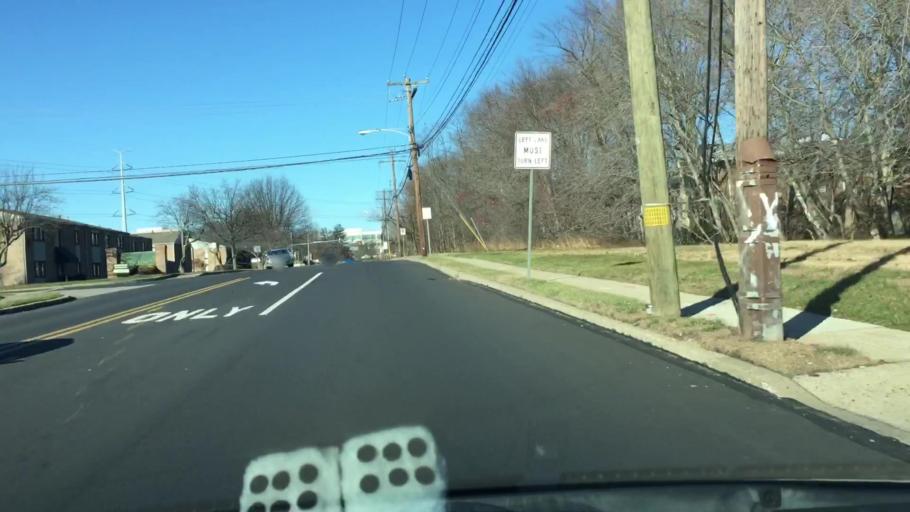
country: US
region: Pennsylvania
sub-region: Montgomery County
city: Horsham
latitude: 40.1631
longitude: -75.1329
